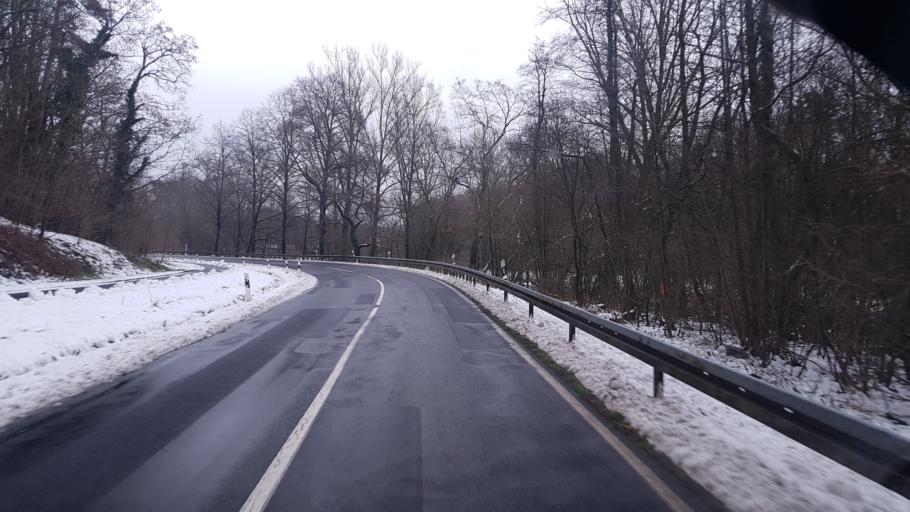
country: DE
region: Brandenburg
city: Lawitz
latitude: 52.1027
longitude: 14.5817
